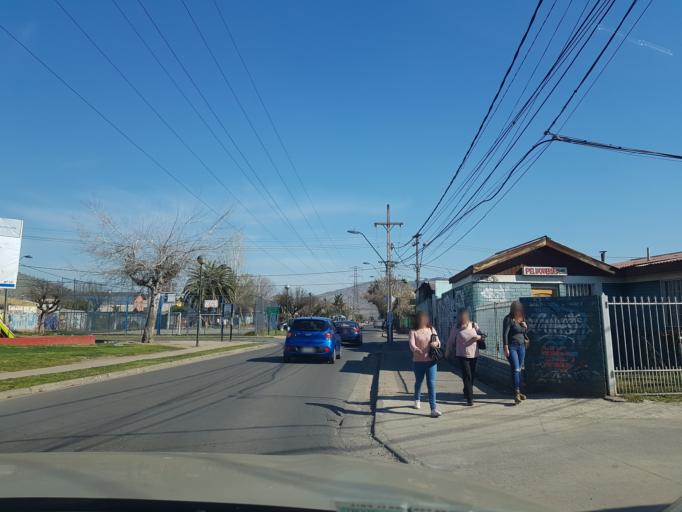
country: CL
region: Santiago Metropolitan
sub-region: Provincia de Santiago
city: Lo Prado
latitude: -33.3687
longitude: -70.7204
